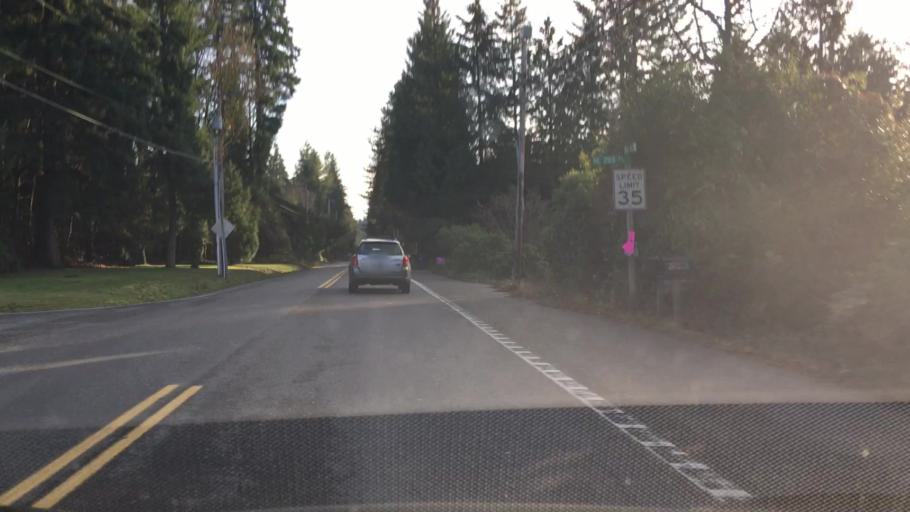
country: US
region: Washington
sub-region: Snohomish County
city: Maltby
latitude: 47.7753
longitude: -122.1318
